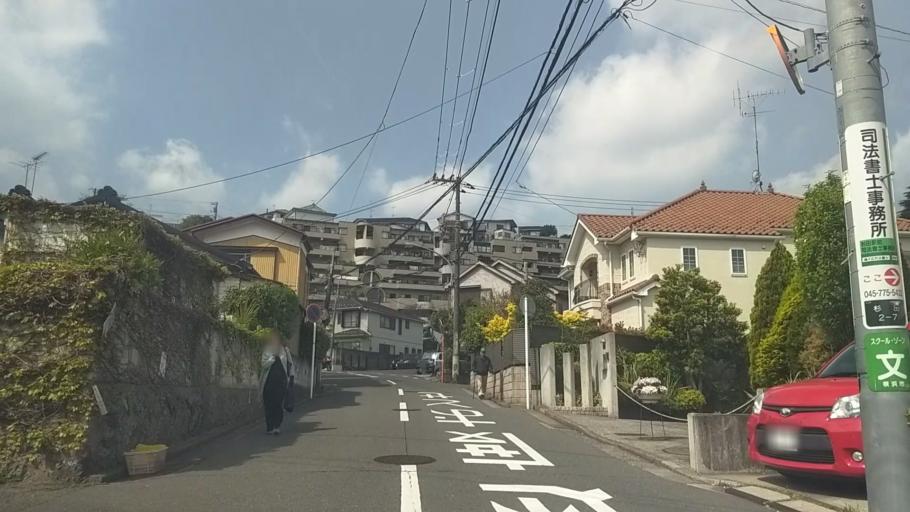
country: JP
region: Kanagawa
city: Yokohama
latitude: 35.3821
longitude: 139.6127
